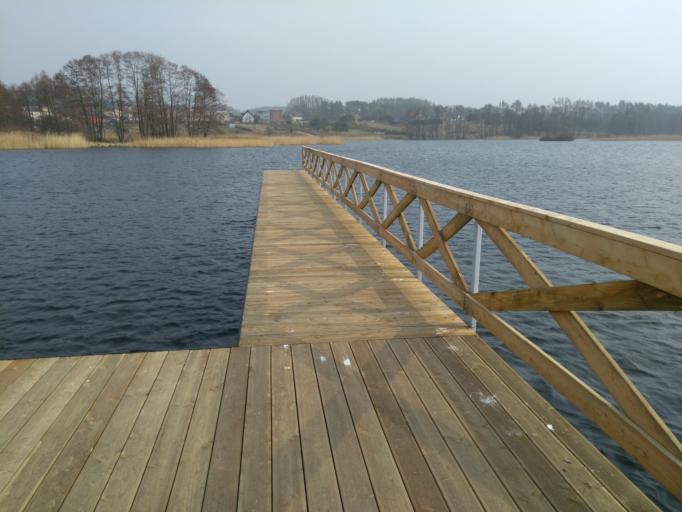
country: PL
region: Pomeranian Voivodeship
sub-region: Powiat kartuski
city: Suleczyno
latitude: 54.3223
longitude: 17.7921
